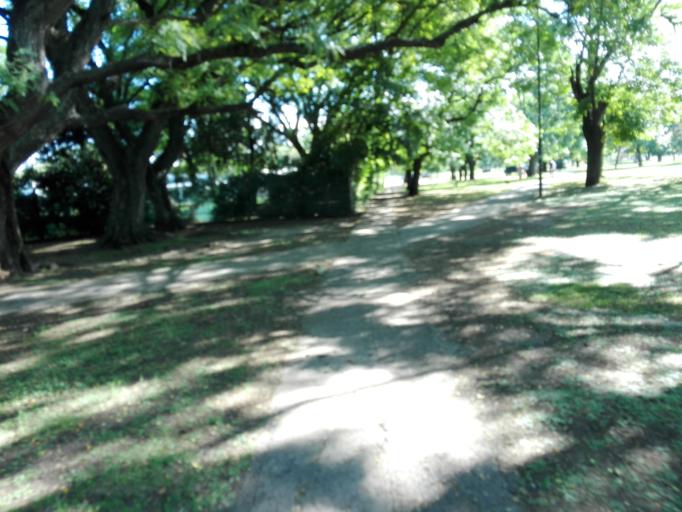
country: AR
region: Buenos Aires
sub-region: Partido de La Plata
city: La Plata
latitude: -34.9310
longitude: -57.9658
